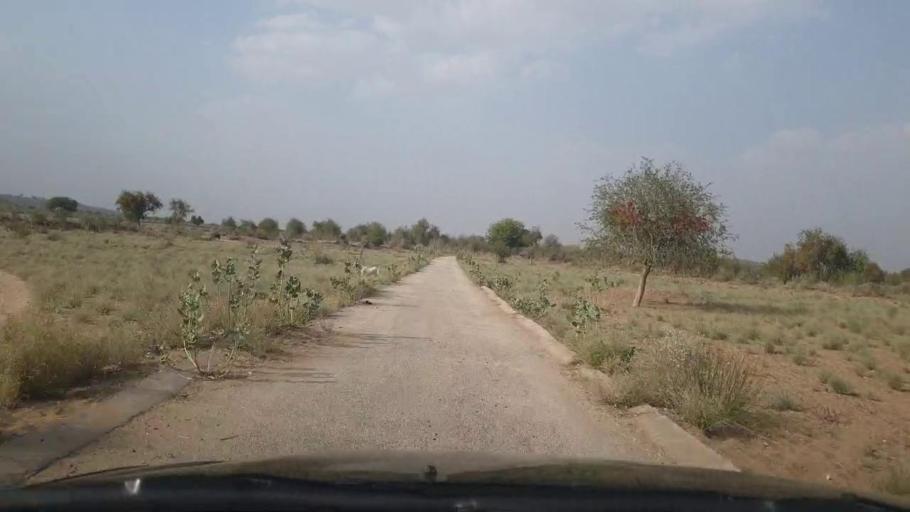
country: PK
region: Sindh
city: Islamkot
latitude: 25.0308
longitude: 70.5589
